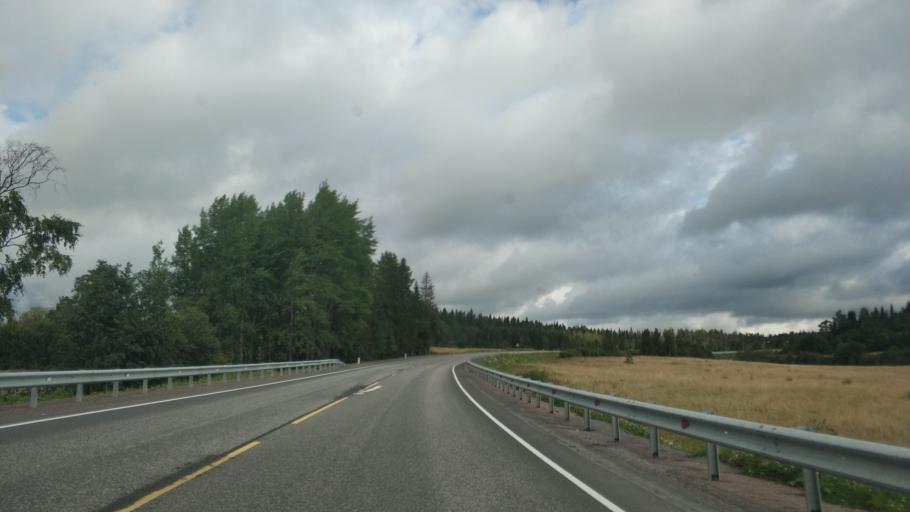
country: RU
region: Republic of Karelia
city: Khelyulya
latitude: 61.7972
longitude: 30.6171
